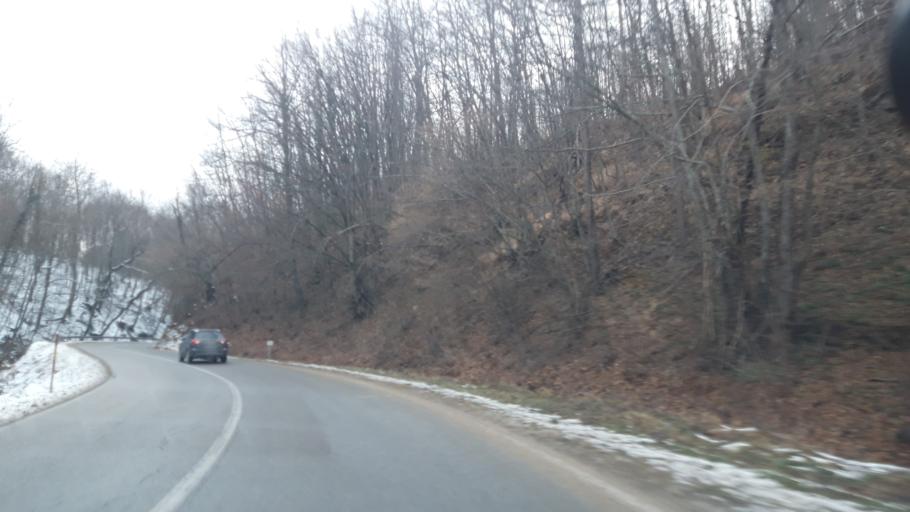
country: BA
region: Republika Srpska
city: Vlasenica
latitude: 44.1829
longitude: 19.0073
